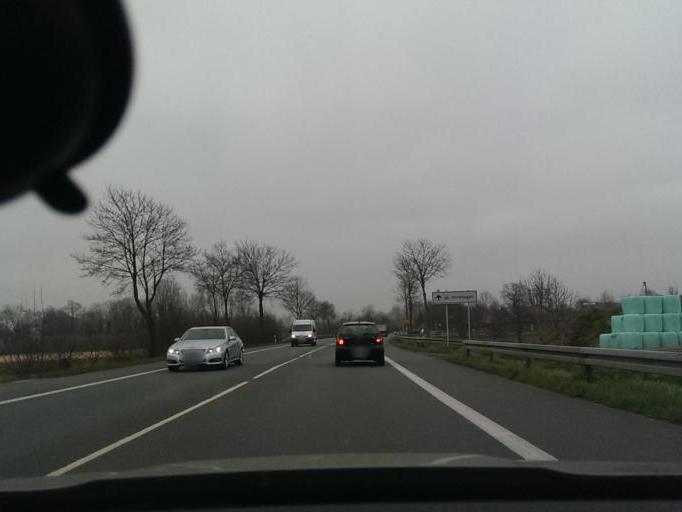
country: DE
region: North Rhine-Westphalia
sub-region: Regierungsbezirk Detmold
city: Delbruck
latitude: 51.7767
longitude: 8.5202
